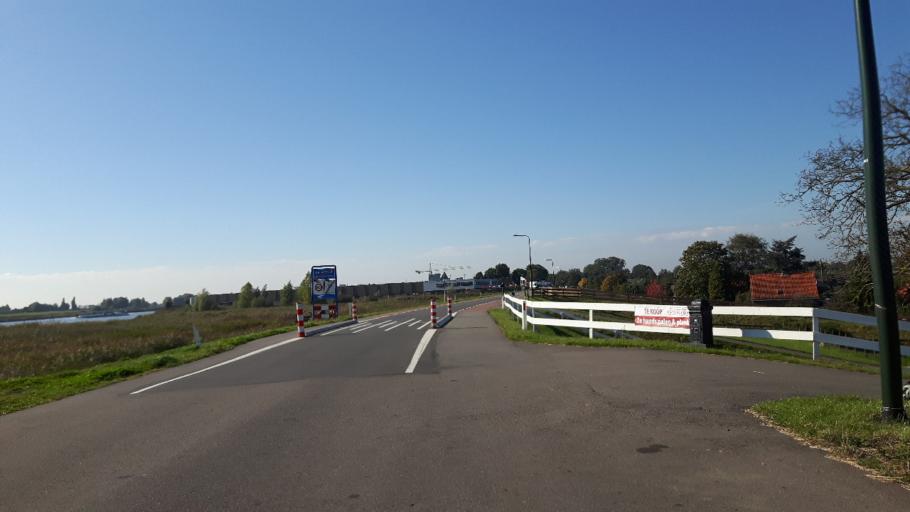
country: NL
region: South Holland
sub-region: Molenwaard
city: Liesveld
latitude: 51.9244
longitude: 4.8014
